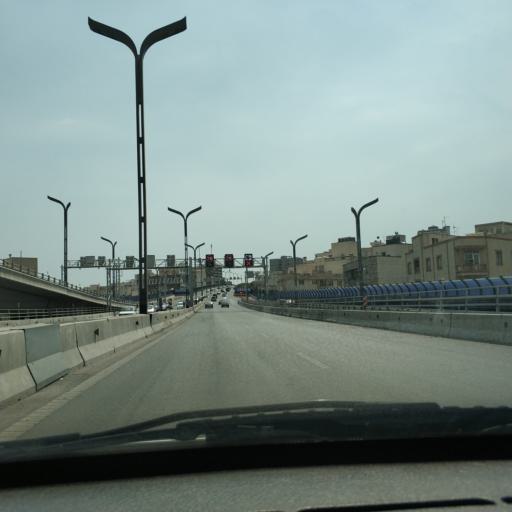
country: IR
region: Tehran
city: Tajrish
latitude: 35.7909
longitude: 51.4554
